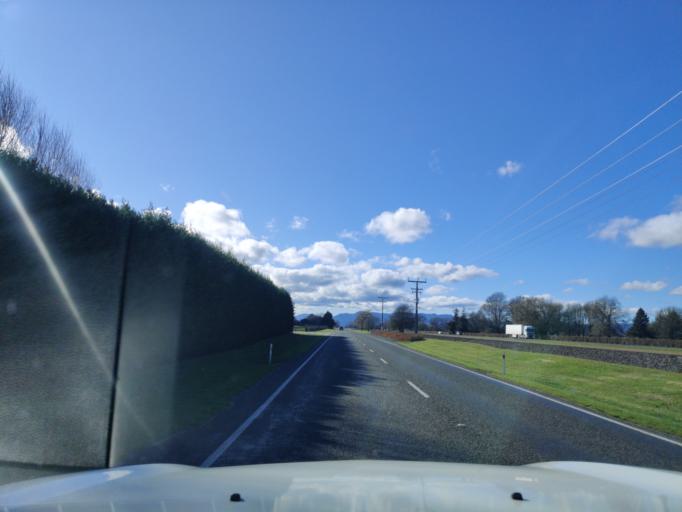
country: NZ
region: Waikato
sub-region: Matamata-Piako District
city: Matamata
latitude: -37.8493
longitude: 175.7597
